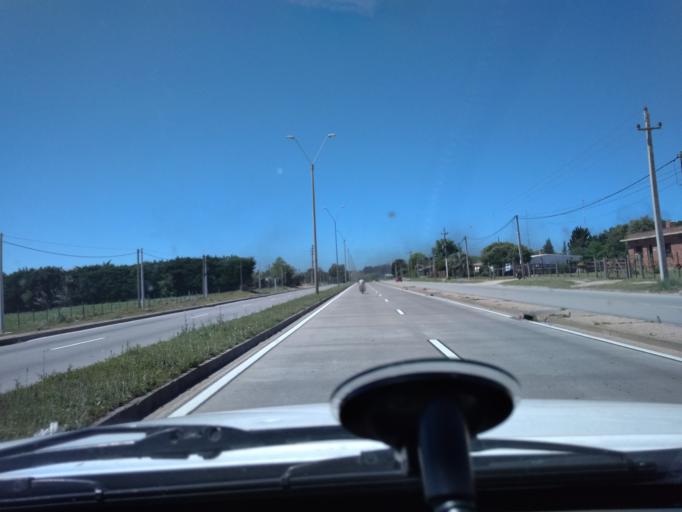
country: UY
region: Canelones
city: Toledo
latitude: -34.7932
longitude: -56.1162
